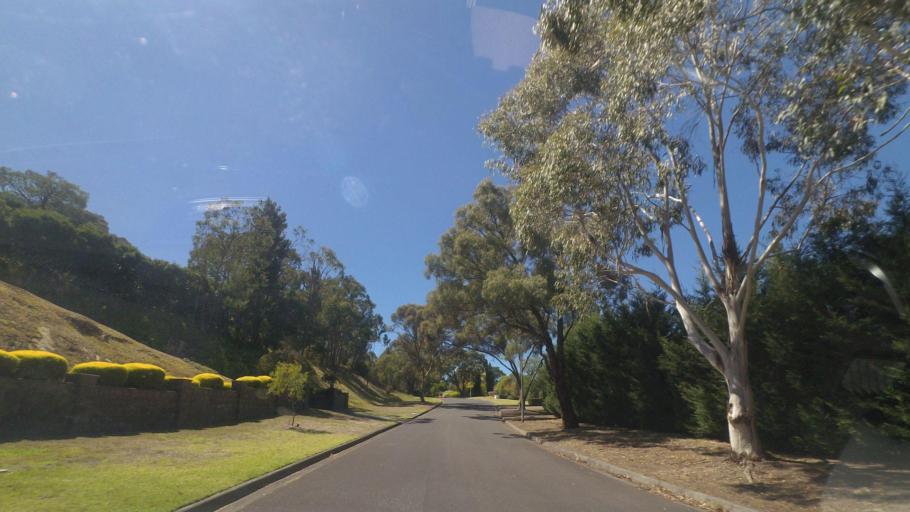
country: AU
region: Victoria
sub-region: Manningham
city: Donvale
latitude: -37.7852
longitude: 145.1900
